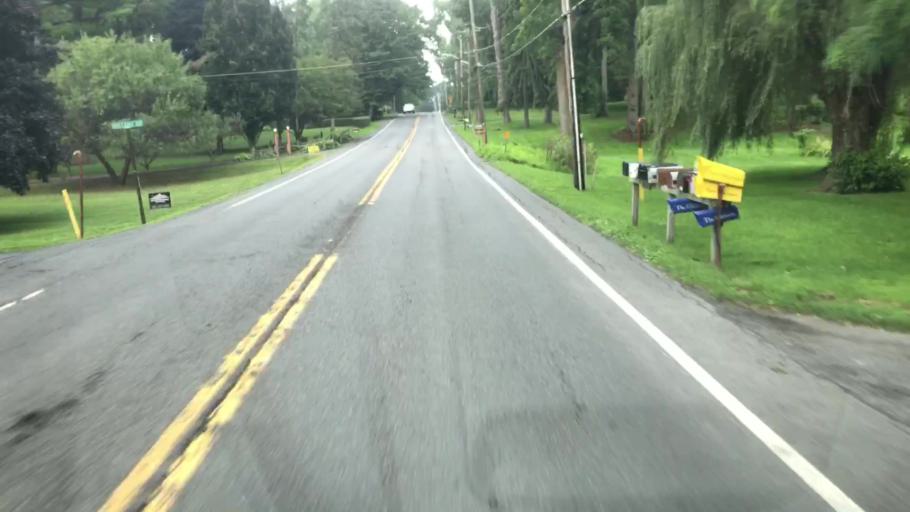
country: US
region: New York
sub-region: Cayuga County
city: Melrose Park
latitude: 42.8986
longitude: -76.5491
